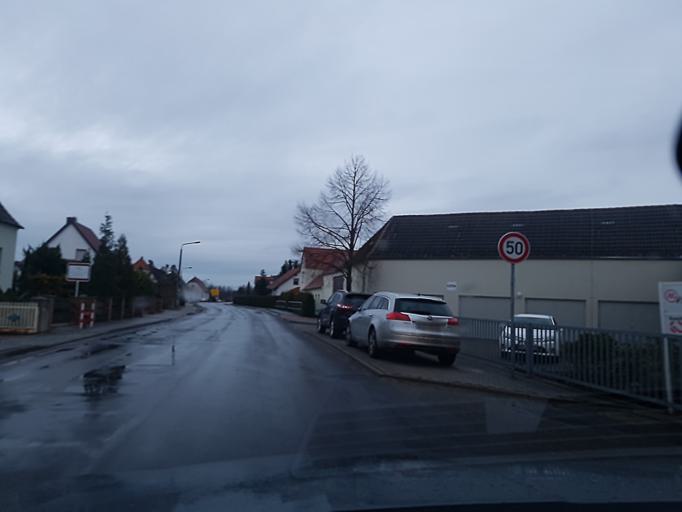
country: DE
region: Brandenburg
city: Falkenberg
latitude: 51.5980
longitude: 13.3067
